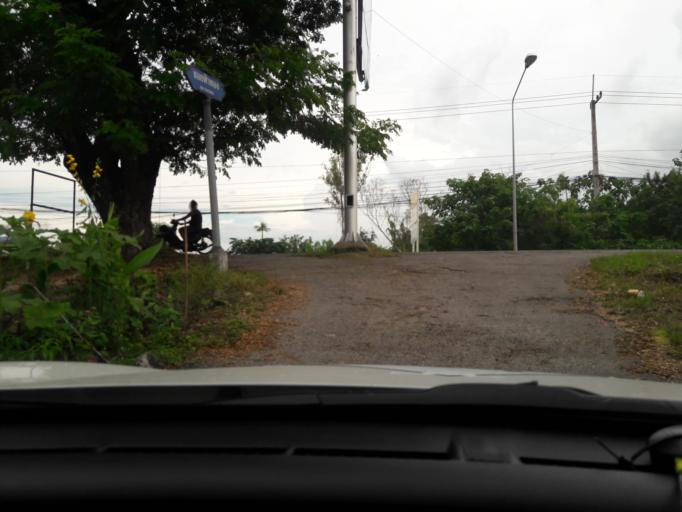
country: TH
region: Nakhon Sawan
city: Tak Fa
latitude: 15.3500
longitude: 100.4994
